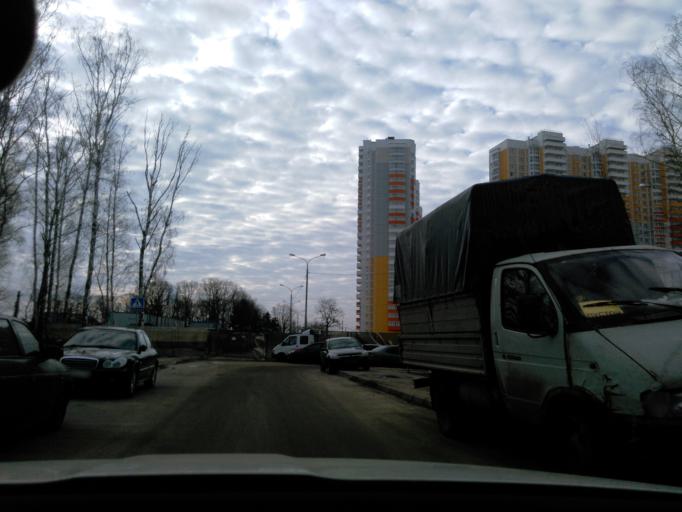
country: RU
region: Moskovskaya
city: Levoberezhnaya
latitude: 55.9032
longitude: 37.4796
